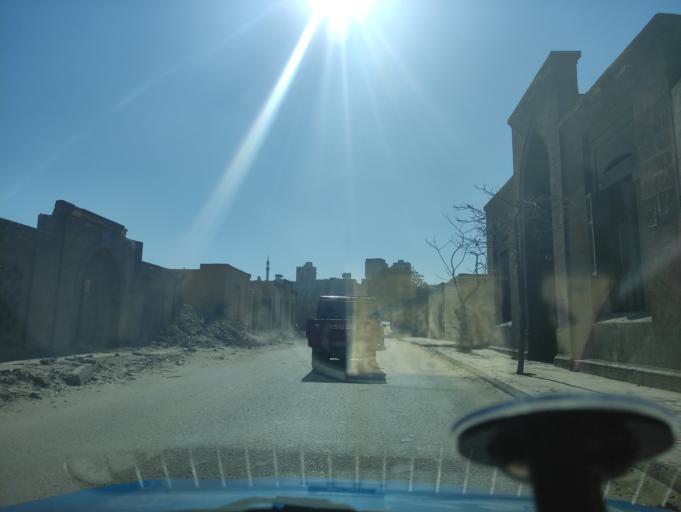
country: EG
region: Muhafazat al Qahirah
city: Cairo
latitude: 30.0497
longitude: 31.2807
